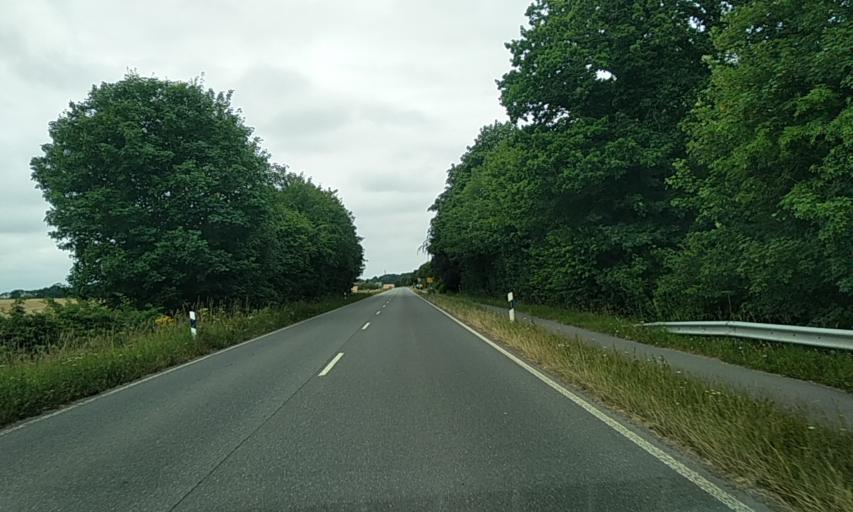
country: DE
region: Schleswig-Holstein
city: Maasholm
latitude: 54.6615
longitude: 9.9900
